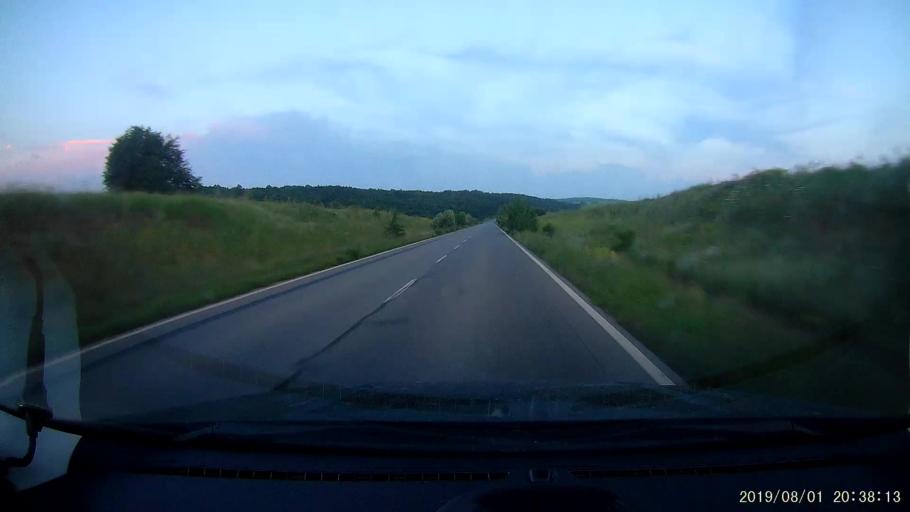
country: BG
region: Yambol
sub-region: Obshtina Elkhovo
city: Elkhovo
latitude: 42.0313
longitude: 26.5994
